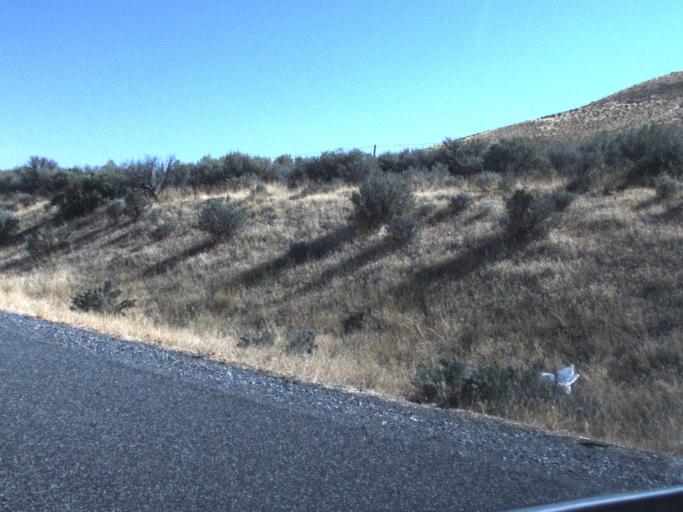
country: US
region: Washington
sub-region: Benton County
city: Richland
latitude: 46.2467
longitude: -119.3309
